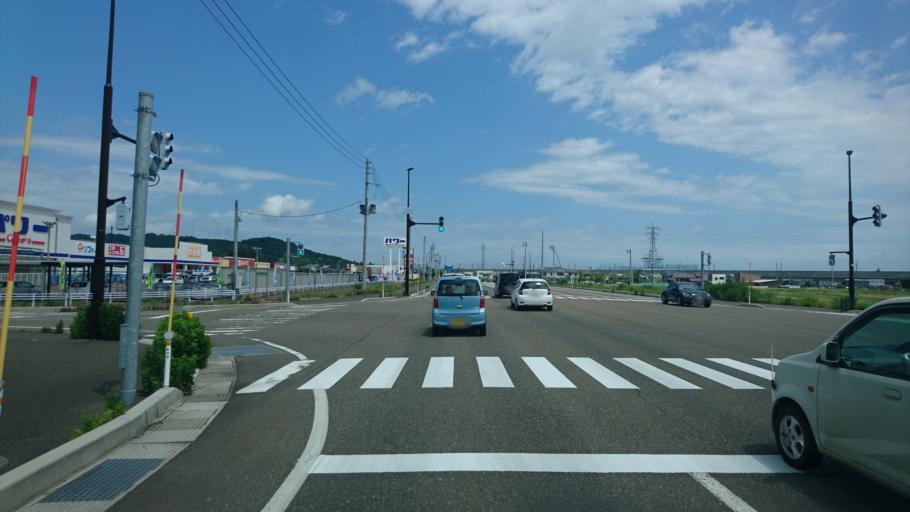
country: JP
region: Niigata
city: Joetsu
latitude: 37.0883
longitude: 138.2335
